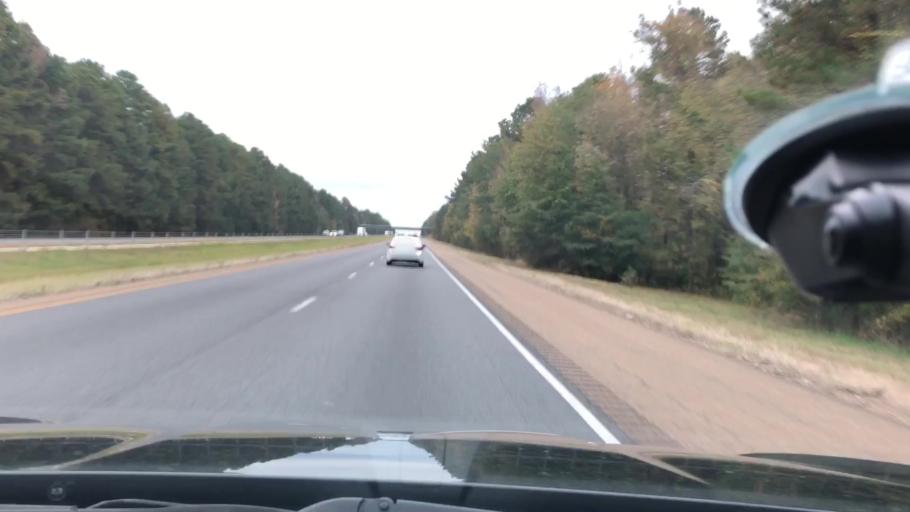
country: US
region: Arkansas
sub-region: Clark County
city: Gurdon
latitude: 33.9677
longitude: -93.2125
